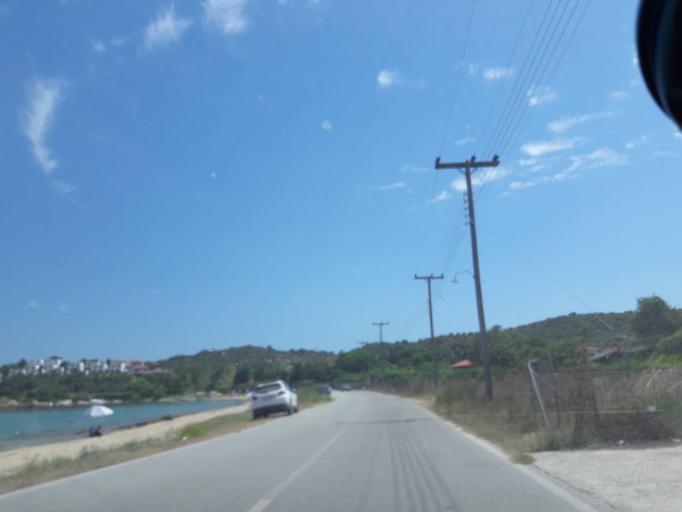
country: GR
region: Central Macedonia
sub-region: Nomos Chalkidikis
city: Ouranoupolis
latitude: 40.3178
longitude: 23.9241
